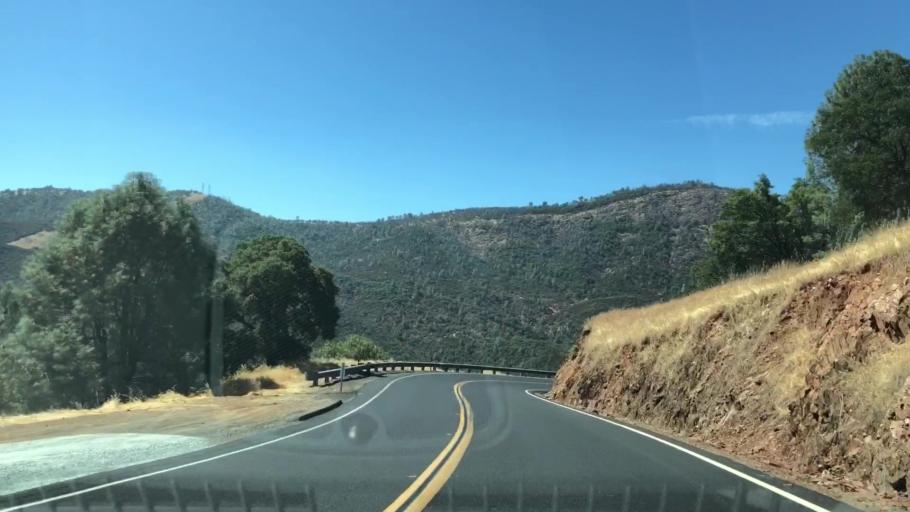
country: US
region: California
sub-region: Tuolumne County
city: Tuolumne City
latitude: 37.8196
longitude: -120.3033
